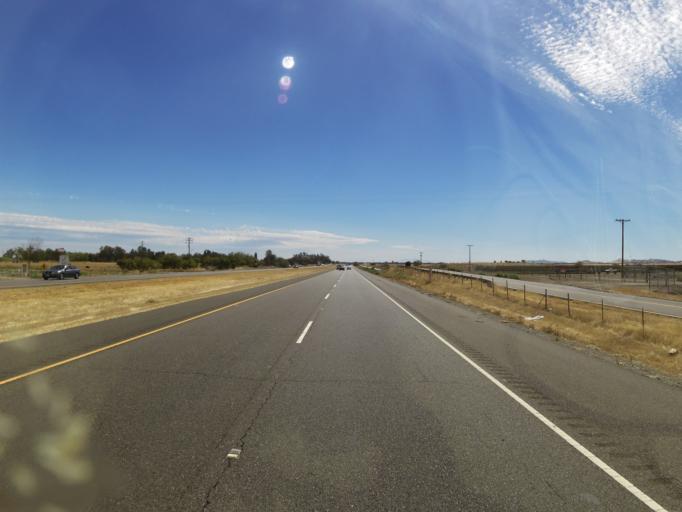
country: US
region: California
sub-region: Solano County
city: Allendale
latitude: 38.4865
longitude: -121.9477
